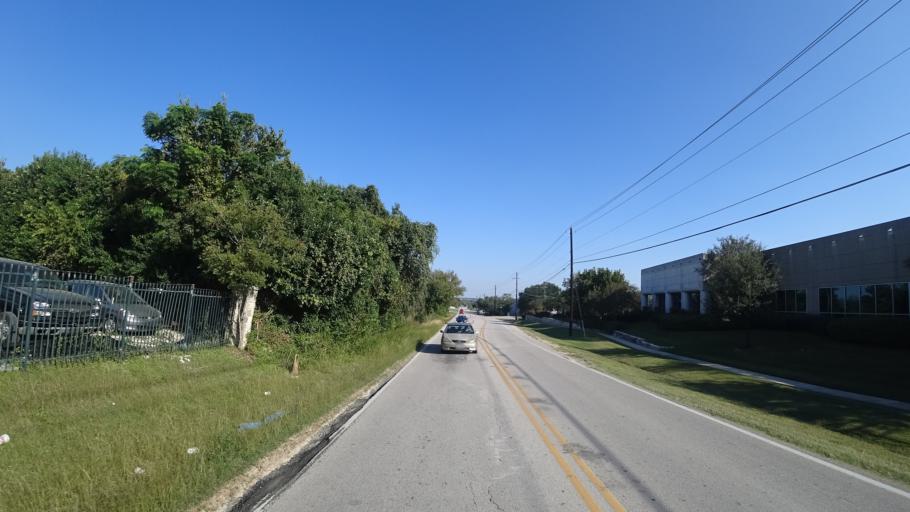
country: US
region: Texas
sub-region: Travis County
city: Wells Branch
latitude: 30.3450
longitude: -97.6695
